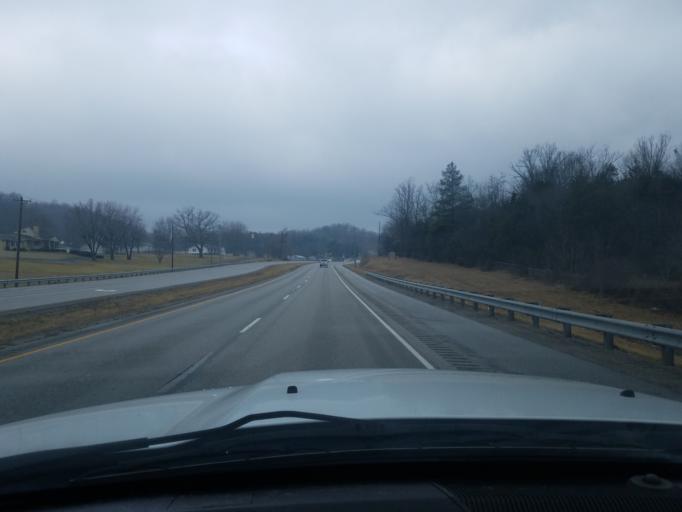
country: US
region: Kentucky
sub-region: Logan County
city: Russellville
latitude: 36.8407
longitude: -86.8514
